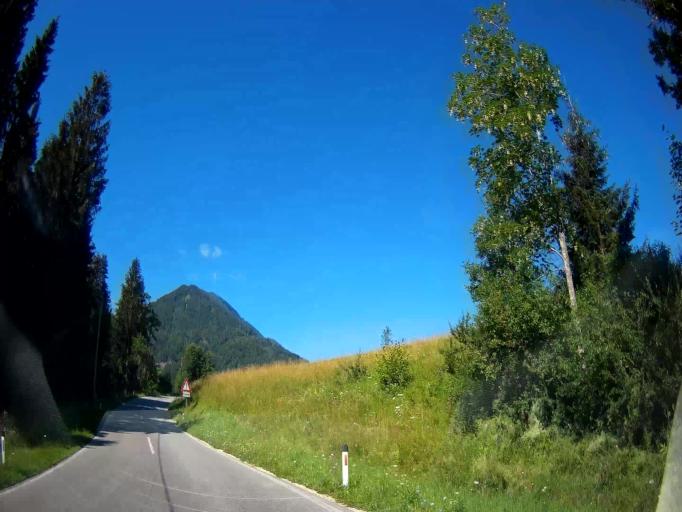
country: AT
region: Carinthia
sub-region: Politischer Bezirk Volkermarkt
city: Gallizien
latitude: 46.5367
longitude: 14.4587
